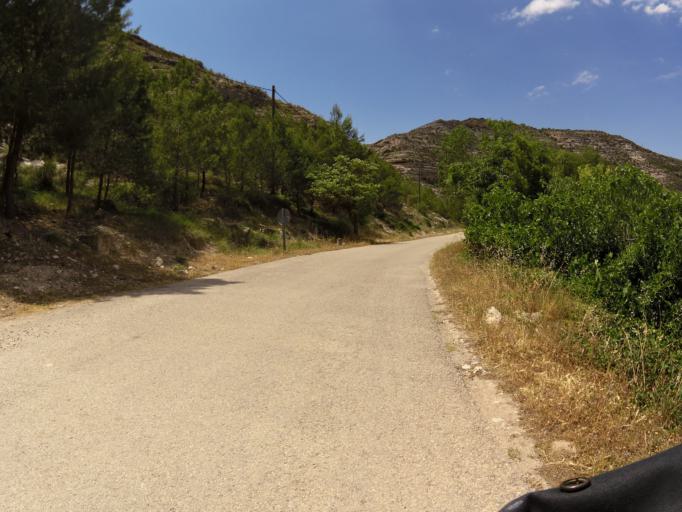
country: ES
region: Castille-La Mancha
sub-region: Provincia de Albacete
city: Jorquera
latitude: 39.1632
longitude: -1.5600
